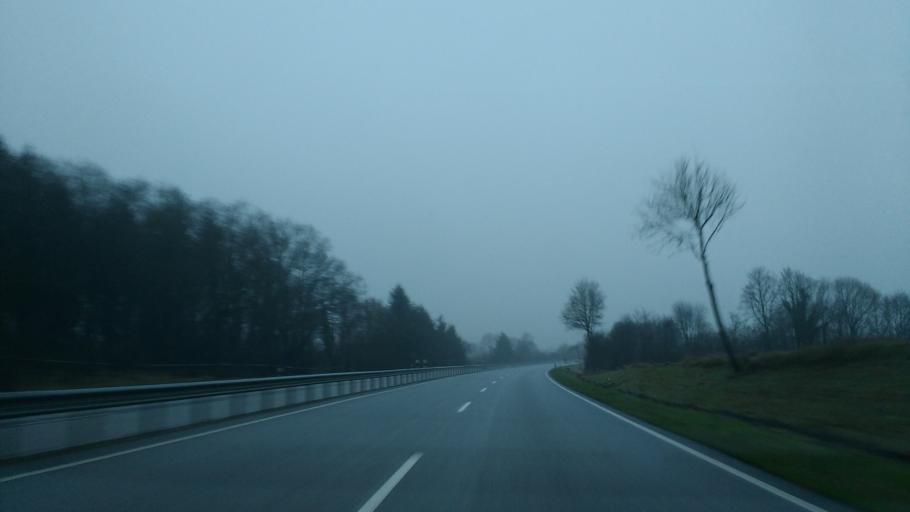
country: DE
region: Schleswig-Holstein
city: Jevenstedt
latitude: 54.2338
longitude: 9.6776
